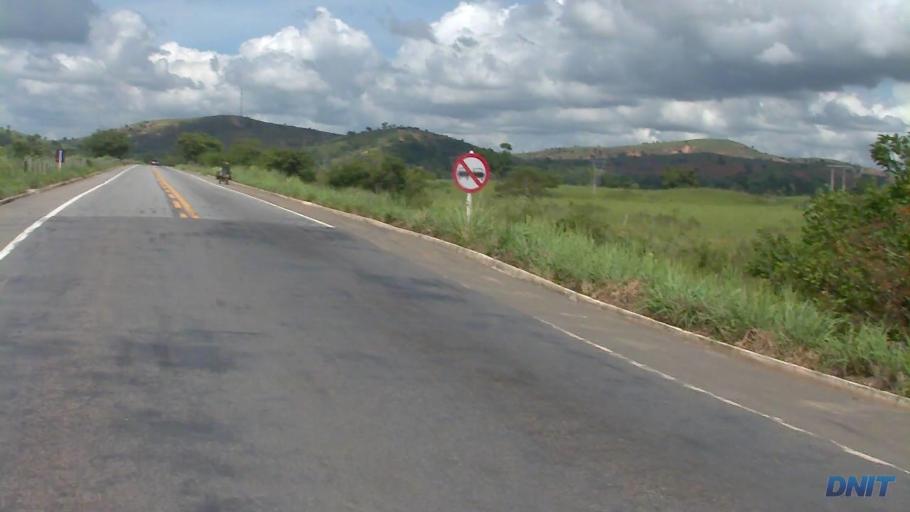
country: BR
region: Minas Gerais
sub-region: Governador Valadares
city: Governador Valadares
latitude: -19.0096
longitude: -42.1364
